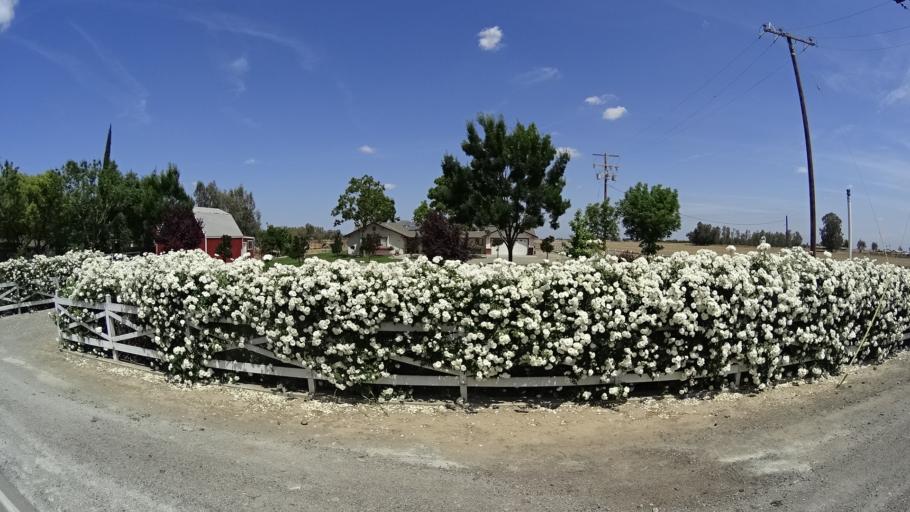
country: US
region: California
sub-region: Kings County
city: Home Garden
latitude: 36.2984
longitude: -119.6146
